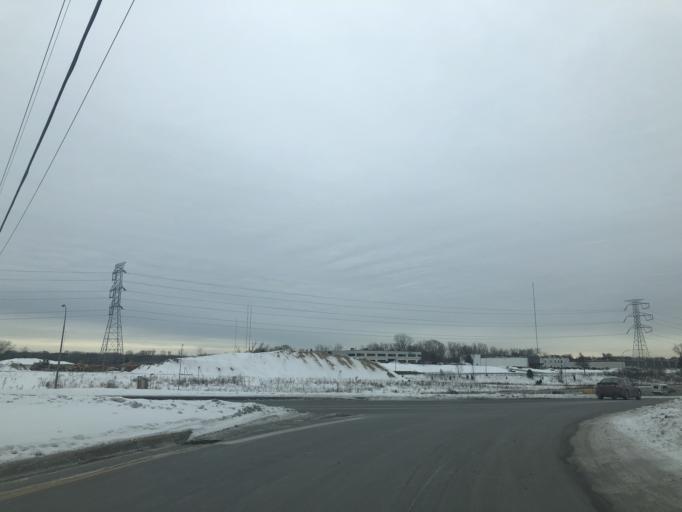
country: US
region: Minnesota
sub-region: Ramsey County
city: New Brighton
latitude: 45.0789
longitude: -93.1867
